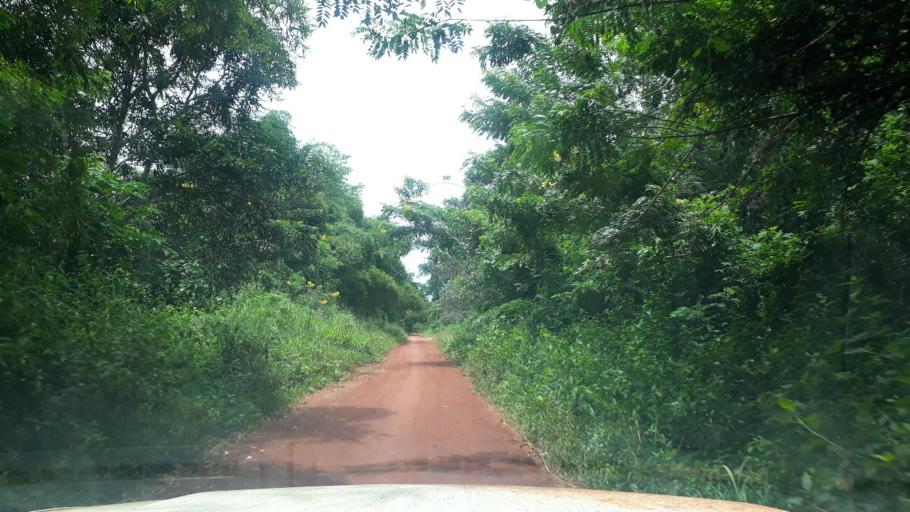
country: CD
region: Eastern Province
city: Aketi
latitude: 2.9339
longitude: 24.0943
